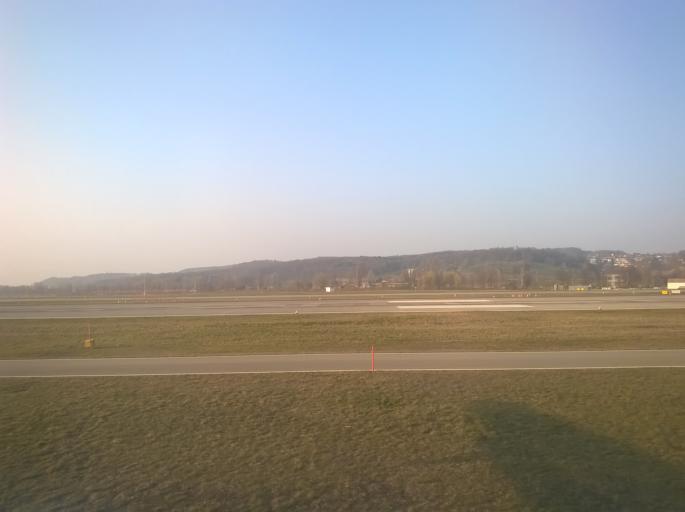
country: CH
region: Zurich
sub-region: Bezirk Buelach
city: Kloten / Holberg
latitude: 47.4557
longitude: 8.5679
